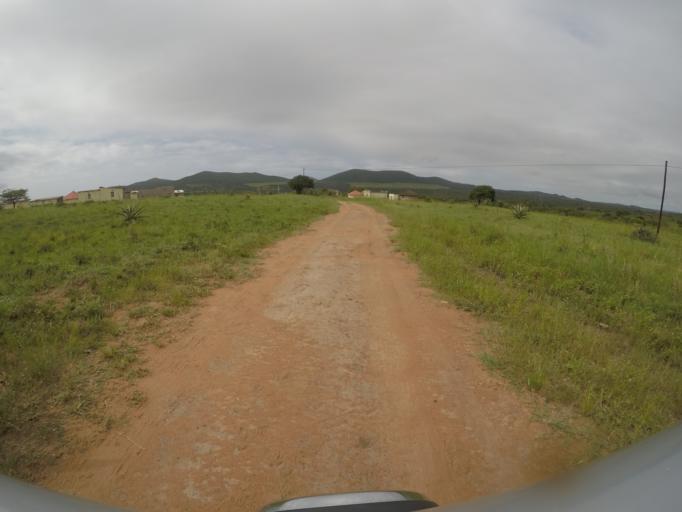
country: ZA
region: KwaZulu-Natal
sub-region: uThungulu District Municipality
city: Empangeni
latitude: -28.6144
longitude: 31.8454
